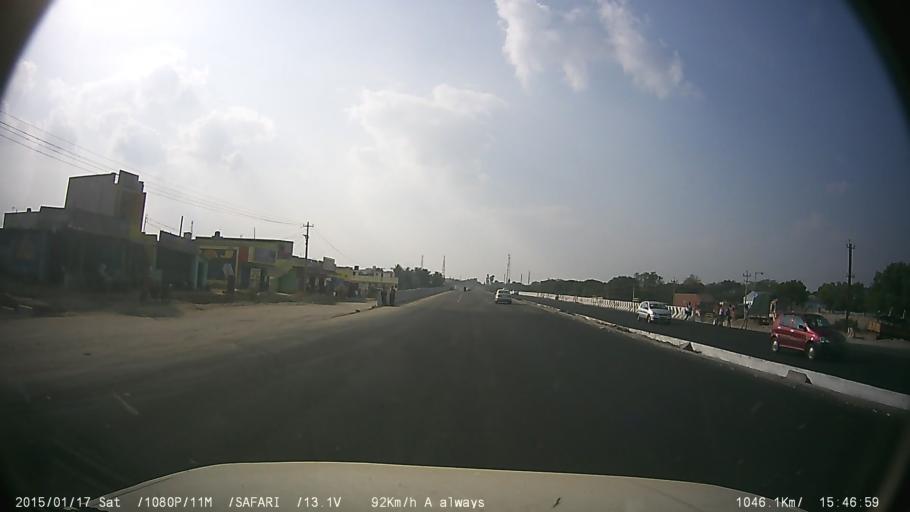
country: IN
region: Tamil Nadu
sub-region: Krishnagiri
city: Hosur
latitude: 12.7161
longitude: 77.8816
